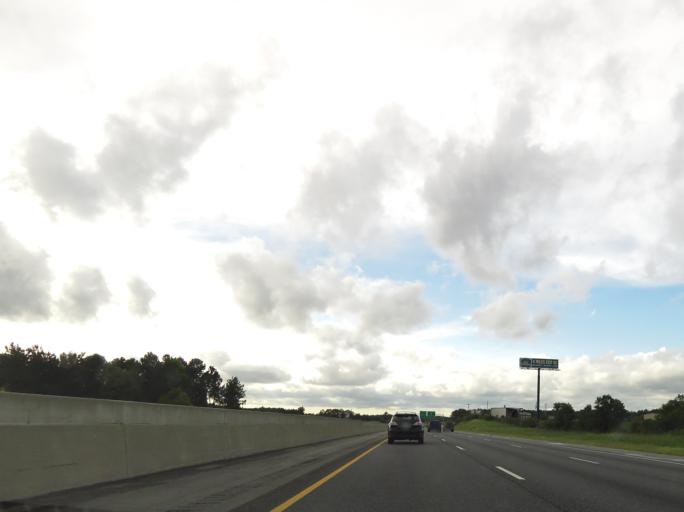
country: US
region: Georgia
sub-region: Turner County
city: Ashburn
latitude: 31.6601
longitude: -83.6032
